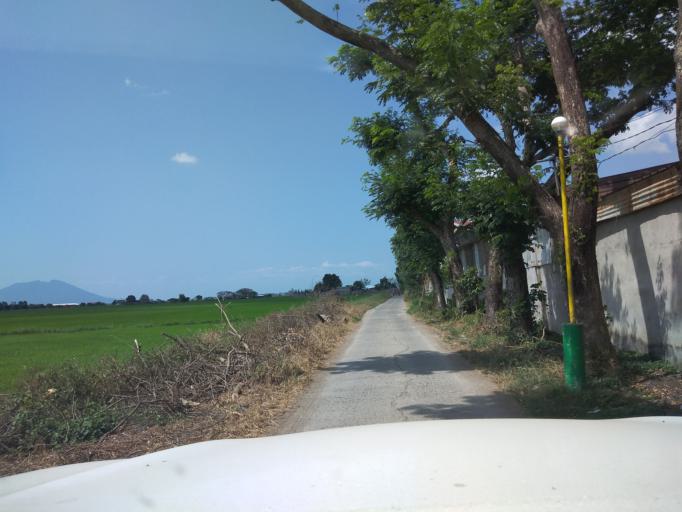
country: PH
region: Central Luzon
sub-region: Province of Pampanga
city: Bahay Pare
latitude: 15.0462
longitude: 120.8806
